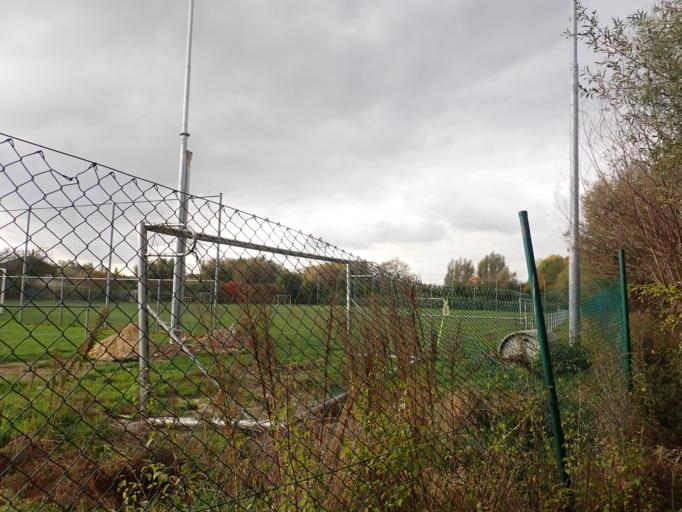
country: BE
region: Flanders
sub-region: Provincie Antwerpen
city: Willebroek
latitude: 51.0602
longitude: 4.3764
